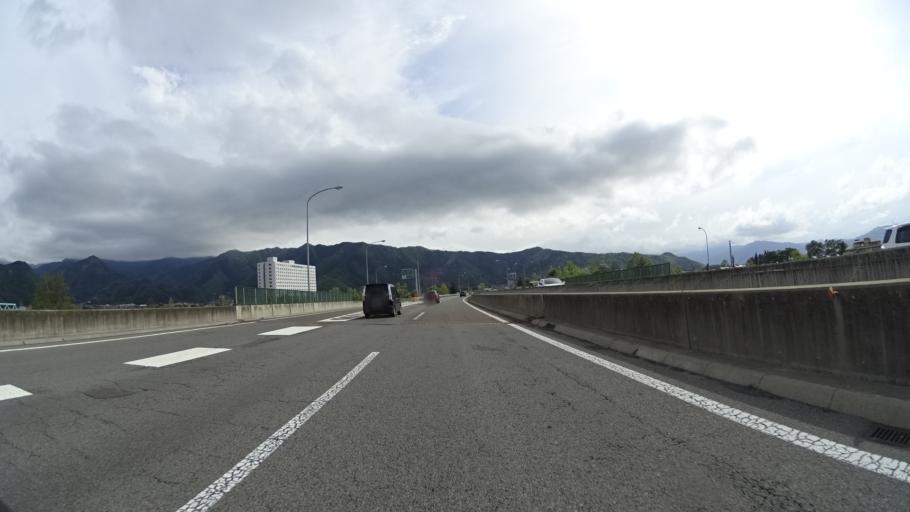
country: JP
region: Nagano
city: Nagano-shi
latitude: 36.5756
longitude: 138.2014
